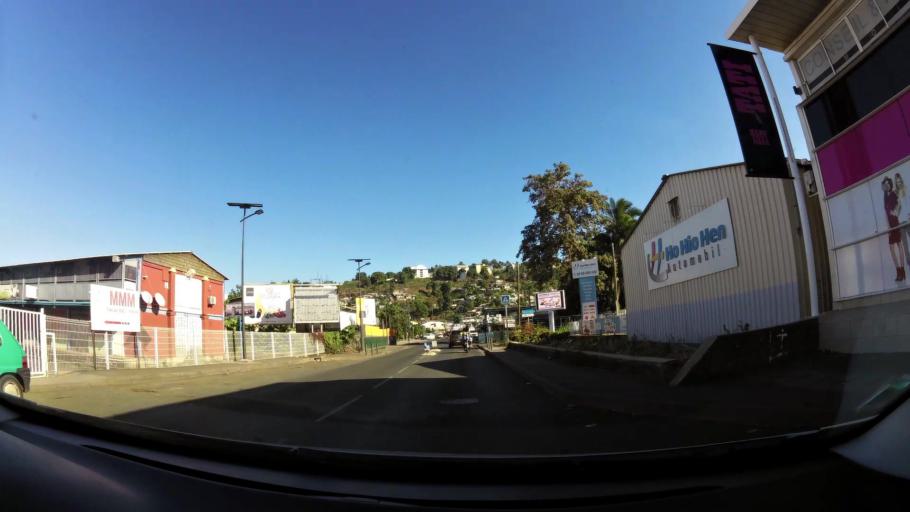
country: YT
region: Mamoudzou
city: Mamoudzou
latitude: -12.7721
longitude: 45.2233
